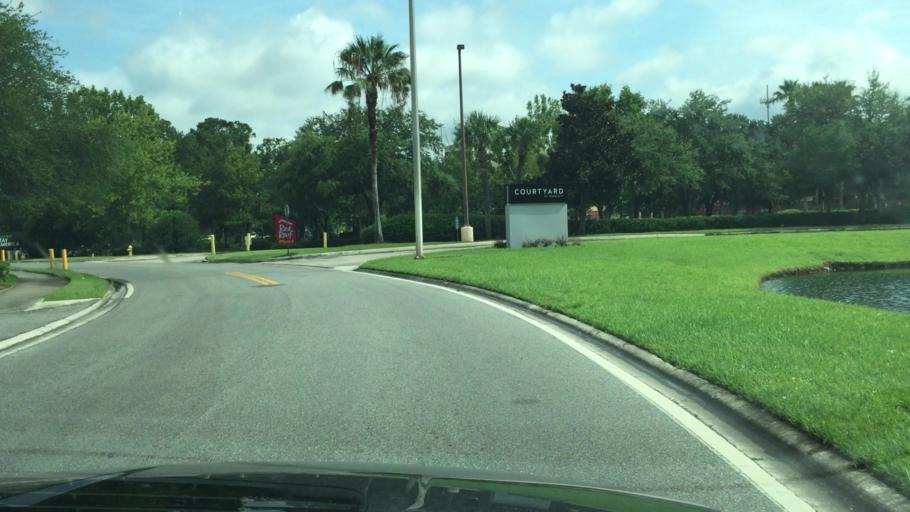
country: US
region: Florida
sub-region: Duval County
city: Jacksonville
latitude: 30.2490
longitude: -81.5976
